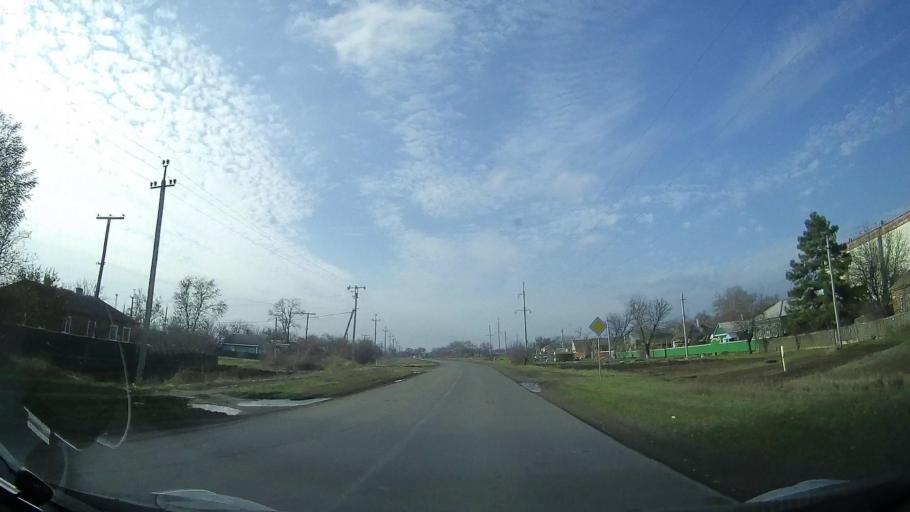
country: RU
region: Rostov
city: Mechetinskaya
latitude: 46.7866
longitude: 40.4774
